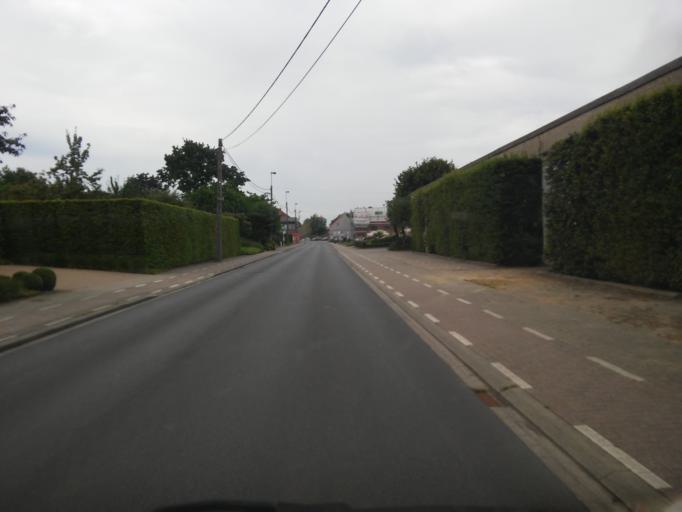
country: BE
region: Flanders
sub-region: Provincie Oost-Vlaanderen
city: Buggenhout
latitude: 51.0216
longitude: 4.1939
